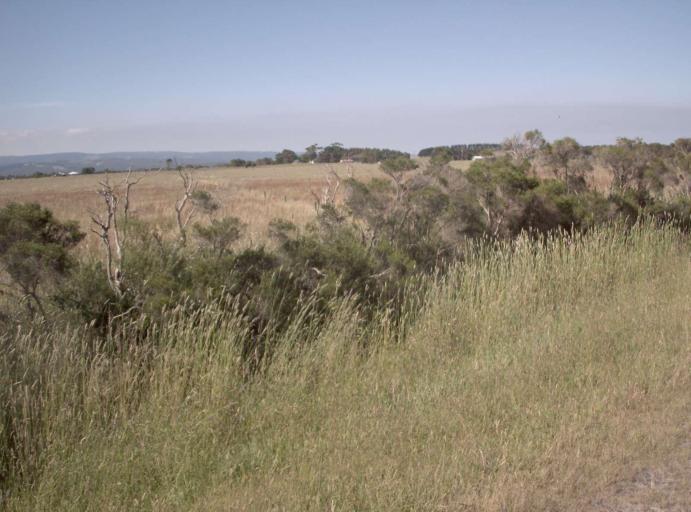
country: AU
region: Victoria
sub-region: Latrobe
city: Traralgon
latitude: -38.6275
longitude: 146.6015
